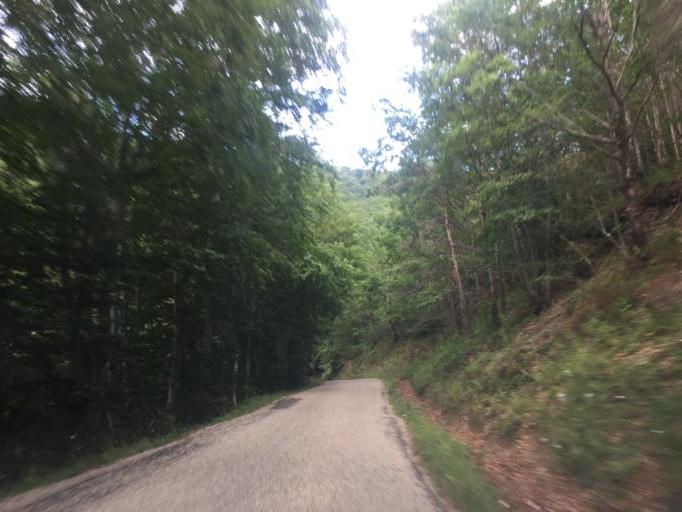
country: FR
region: Rhone-Alpes
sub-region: Departement de l'Ardeche
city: Flaviac
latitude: 44.7885
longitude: 4.6549
